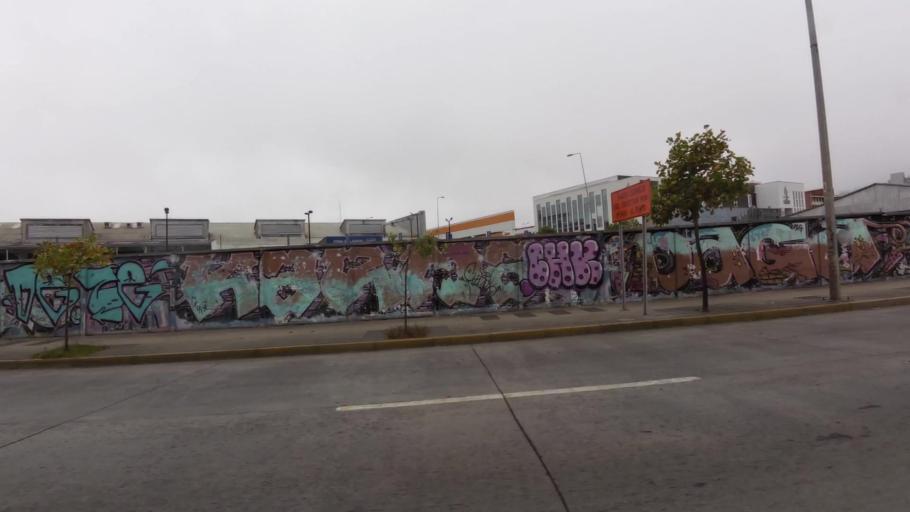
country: CL
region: Biobio
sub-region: Provincia de Concepcion
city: Concepcion
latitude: -36.8252
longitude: -73.0634
